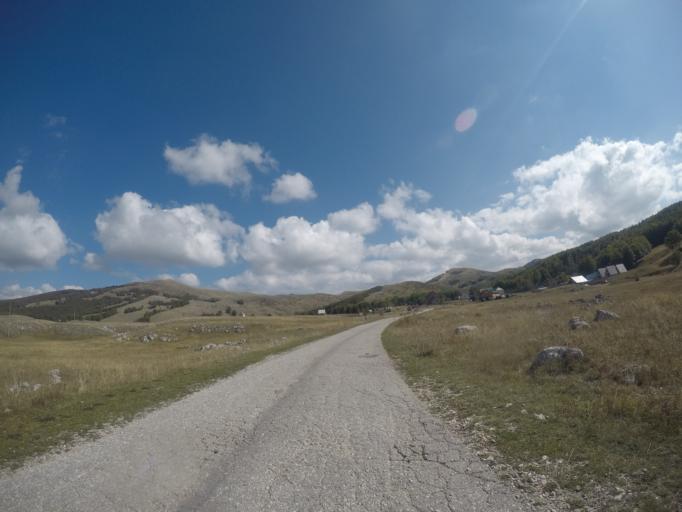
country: ME
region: Opstina Pluzine
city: Pluzine
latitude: 43.1884
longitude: 18.9326
